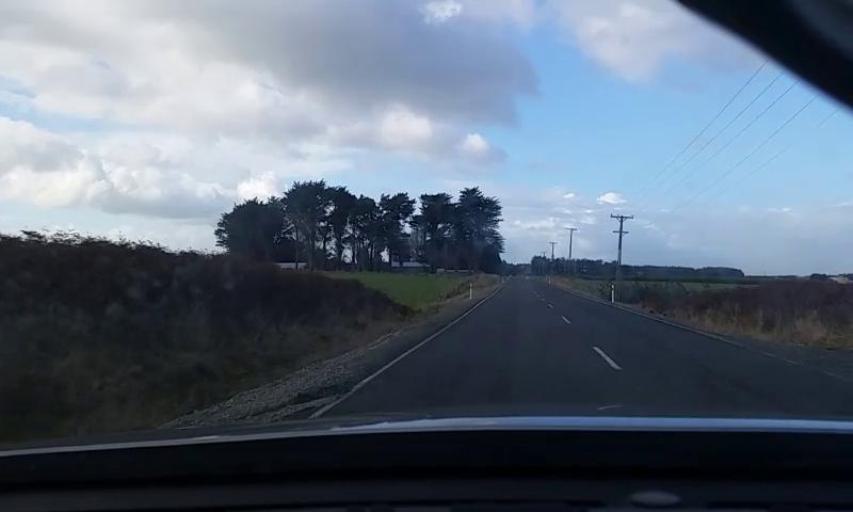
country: NZ
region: Southland
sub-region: Invercargill City
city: Invercargill
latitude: -46.3807
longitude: 168.4186
